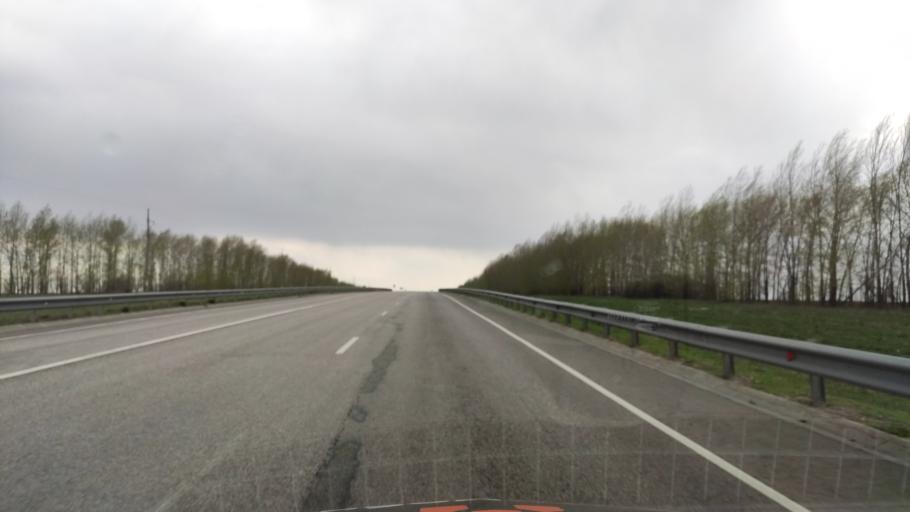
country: RU
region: Voronezj
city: Nizhnedevitsk
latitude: 51.5655
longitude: 38.4588
